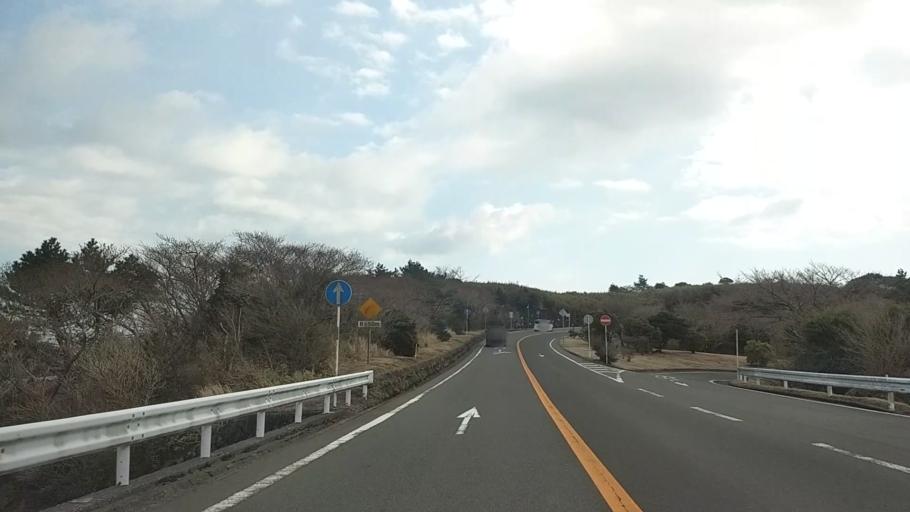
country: JP
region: Shizuoka
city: Atami
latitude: 35.0856
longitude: 139.0326
